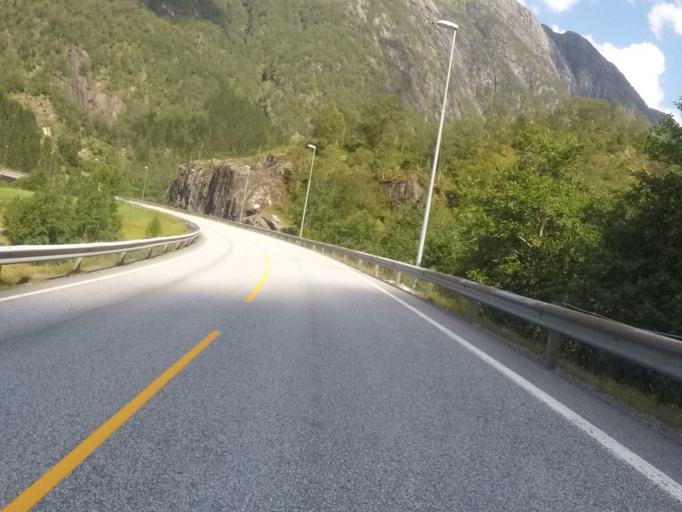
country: NO
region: Hordaland
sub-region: Masfjorden
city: Masfjorden
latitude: 60.9153
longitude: 5.5317
